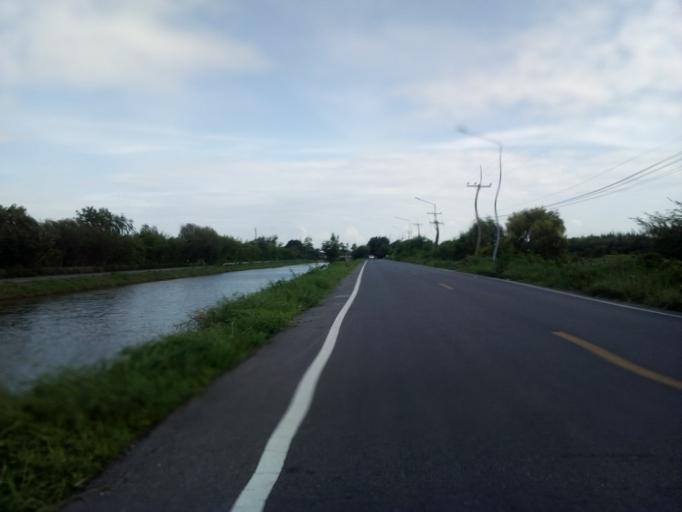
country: TH
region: Pathum Thani
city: Nong Suea
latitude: 14.0649
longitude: 100.8465
